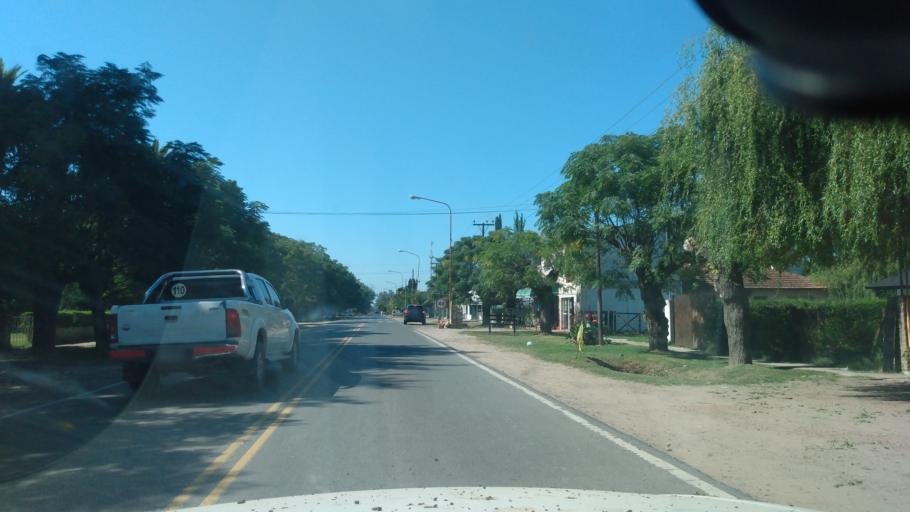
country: AR
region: Buenos Aires
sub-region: Partido de Lujan
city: Lujan
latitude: -34.4935
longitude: -59.0758
